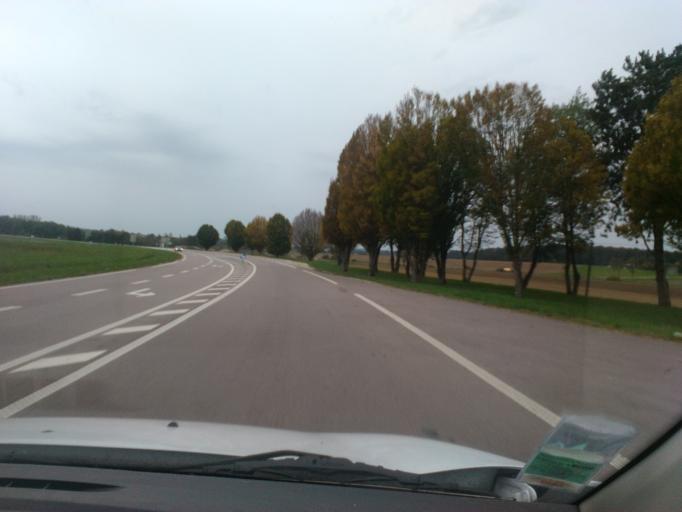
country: FR
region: Lorraine
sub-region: Departement des Vosges
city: Rambervillers
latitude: 48.3254
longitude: 6.6320
